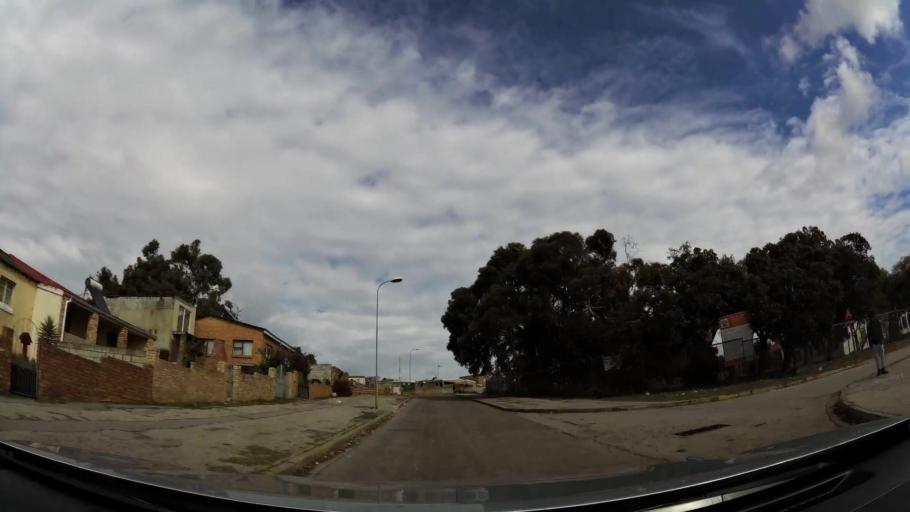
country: ZA
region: Eastern Cape
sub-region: Nelson Mandela Bay Metropolitan Municipality
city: Port Elizabeth
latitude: -33.9300
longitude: 25.5651
